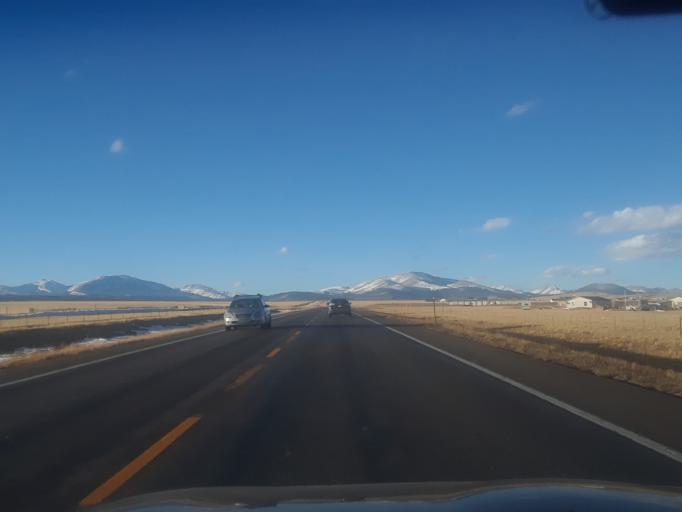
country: US
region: Colorado
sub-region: Park County
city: Fairplay
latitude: 39.1236
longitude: -105.9936
